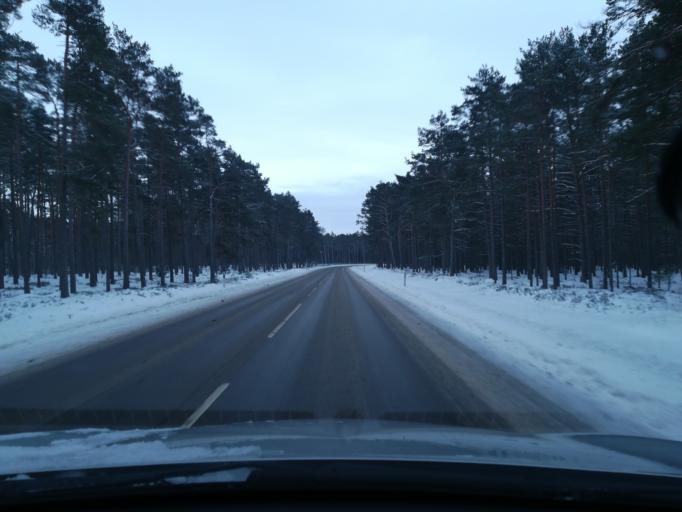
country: EE
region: Harju
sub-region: Keila linn
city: Keila
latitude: 59.4278
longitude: 24.3615
